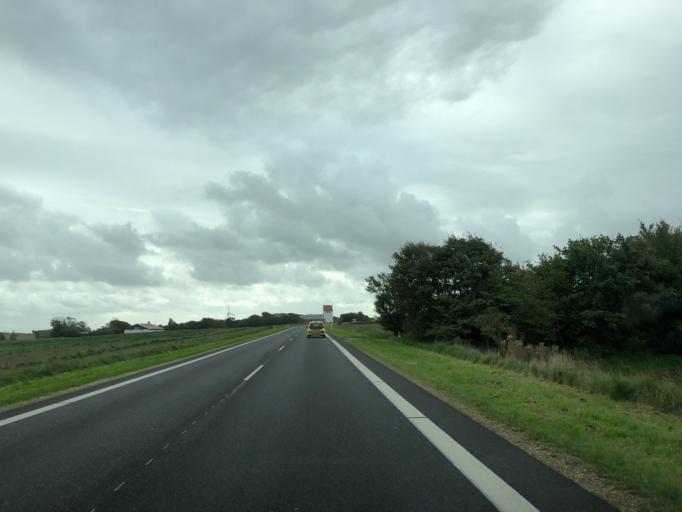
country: DK
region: North Denmark
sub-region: Thisted Kommune
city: Thisted
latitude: 56.8789
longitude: 8.5923
